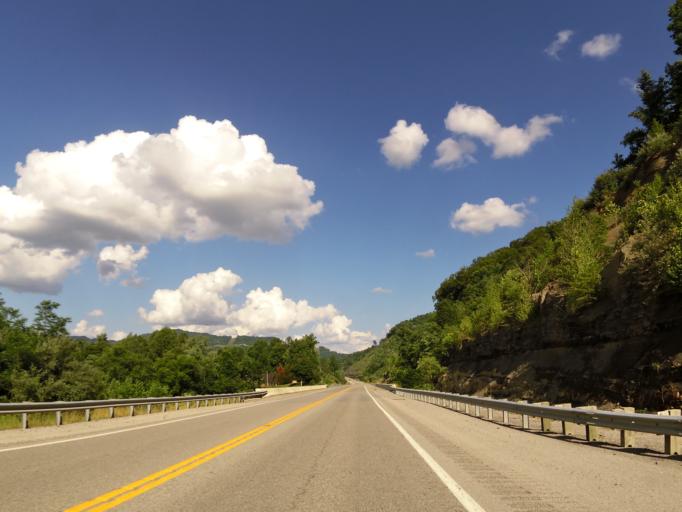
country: US
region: Kentucky
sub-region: Harlan County
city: Harlan
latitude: 36.7840
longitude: -83.2448
